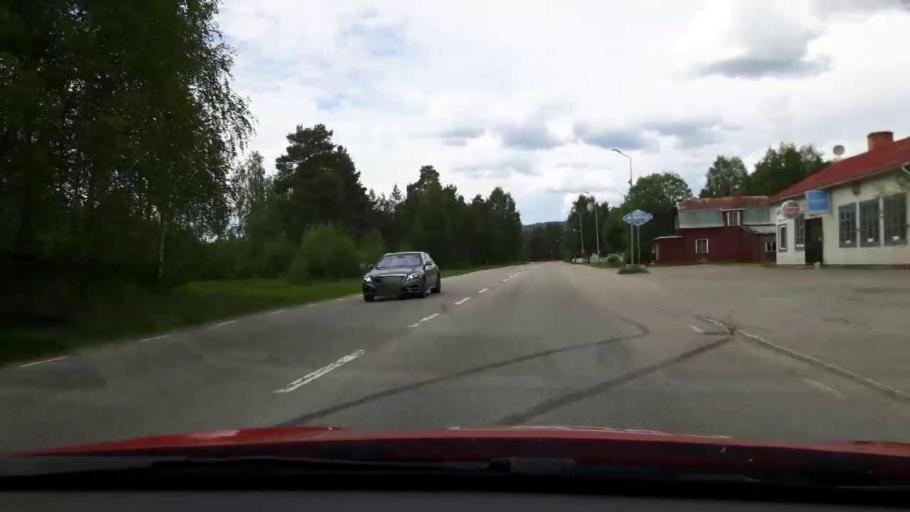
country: SE
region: Jaemtland
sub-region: Harjedalens Kommun
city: Sveg
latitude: 62.4237
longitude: 13.5340
